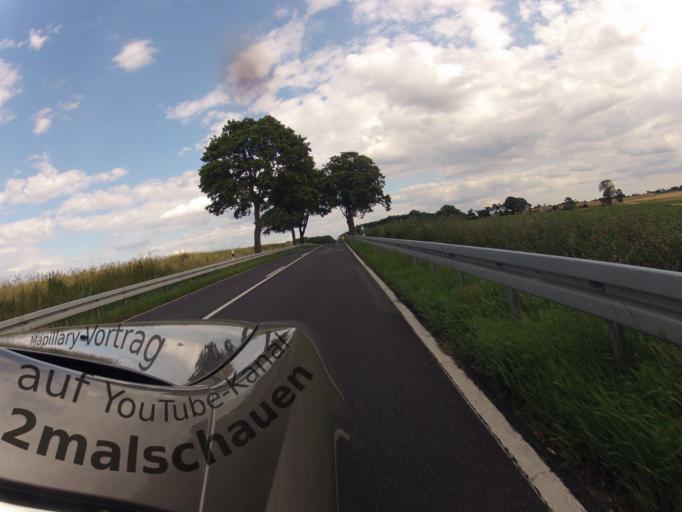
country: DE
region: Mecklenburg-Vorpommern
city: Seebad Bansin
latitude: 53.8994
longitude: 14.0573
